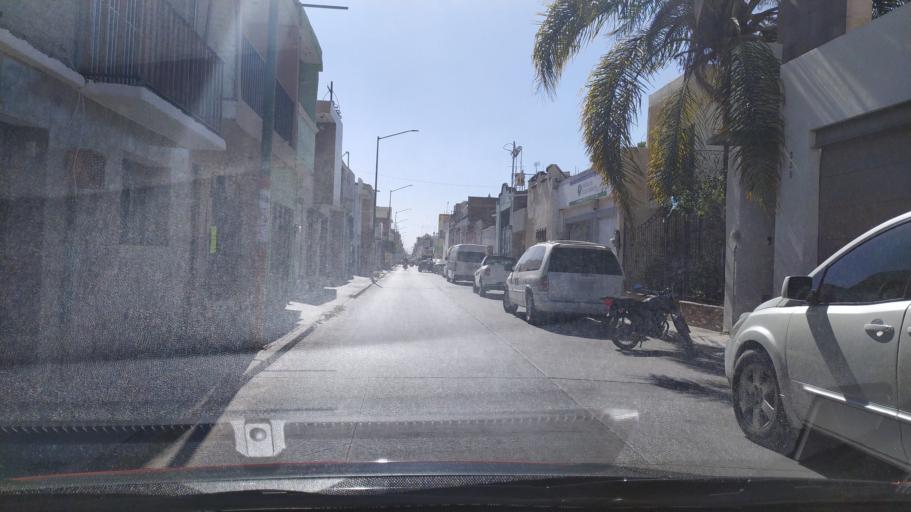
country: MX
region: Guanajuato
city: San Francisco del Rincon
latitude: 21.0227
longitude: -101.8581
